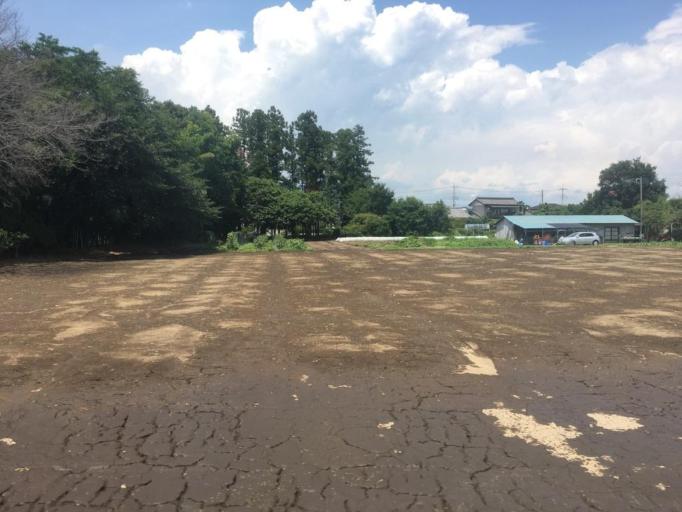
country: JP
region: Gunma
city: Omamacho-omama
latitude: 36.4131
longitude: 139.1884
